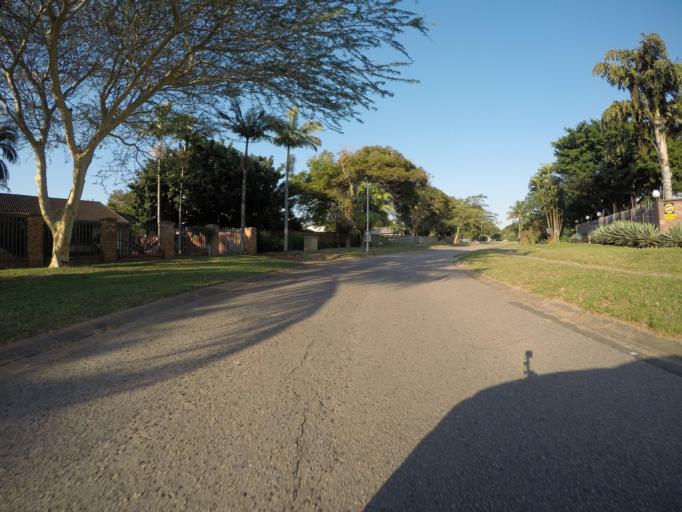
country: ZA
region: KwaZulu-Natal
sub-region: uThungulu District Municipality
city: Richards Bay
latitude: -28.7755
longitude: 32.1072
